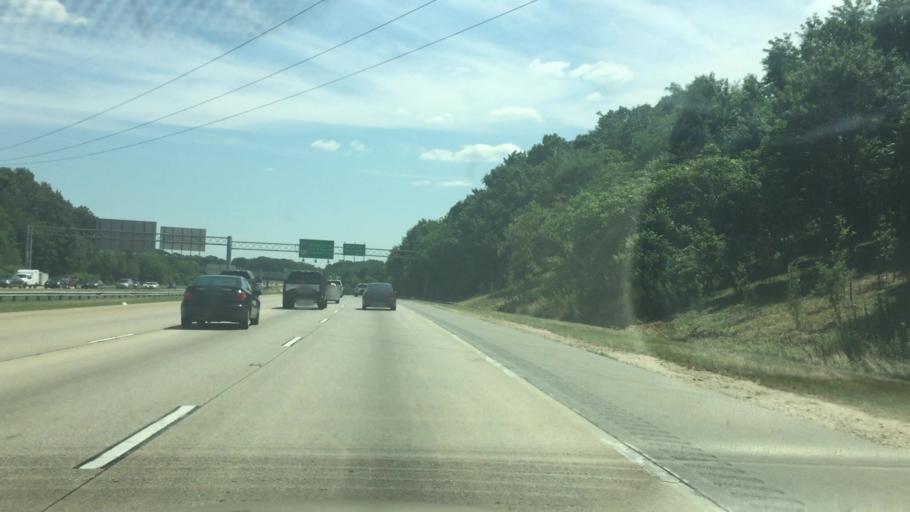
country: US
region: Maryland
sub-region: Anne Arundel County
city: Ferndale
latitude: 39.1914
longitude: -76.6331
